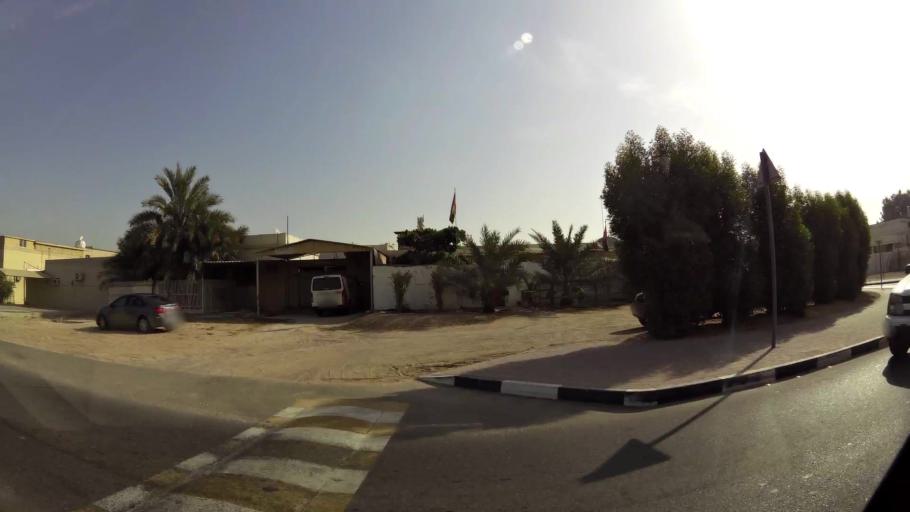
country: AE
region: Ash Shariqah
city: Sharjah
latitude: 25.2186
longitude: 55.3865
